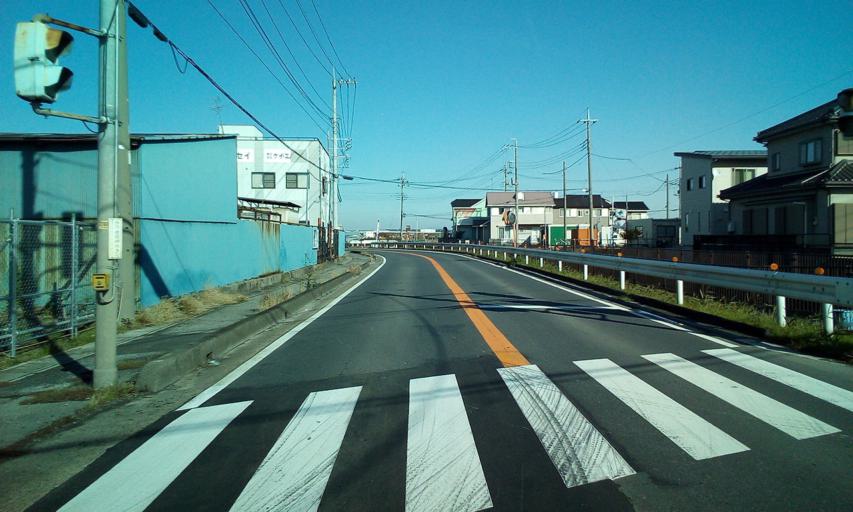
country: JP
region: Chiba
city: Nagareyama
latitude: 35.8631
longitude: 139.8881
